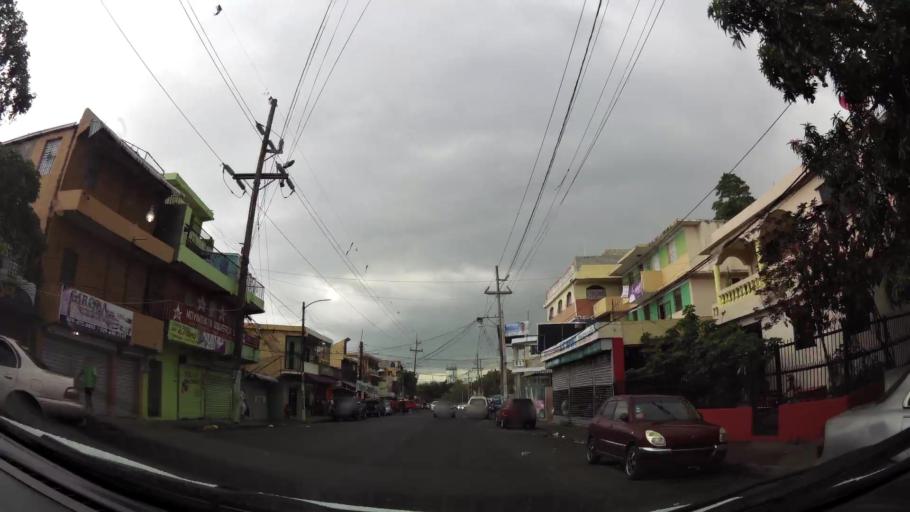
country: DO
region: Nacional
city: La Agustina
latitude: 18.4991
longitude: -69.9270
